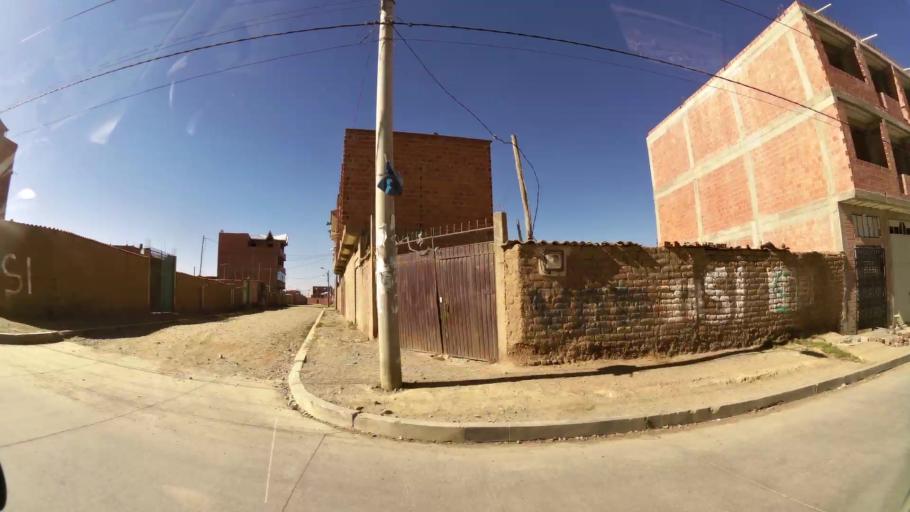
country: BO
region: La Paz
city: La Paz
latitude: -16.5354
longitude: -68.2190
